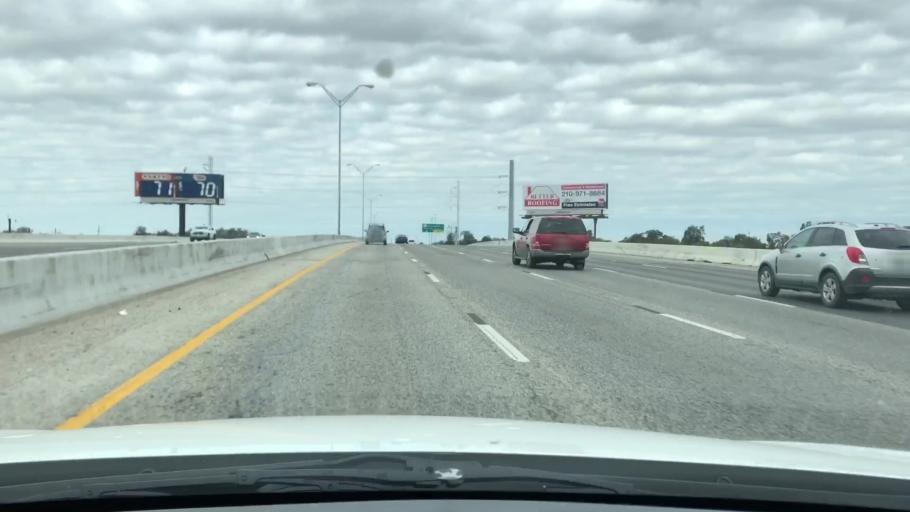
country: US
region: Texas
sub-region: Bexar County
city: San Antonio
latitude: 29.3977
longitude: -98.5276
